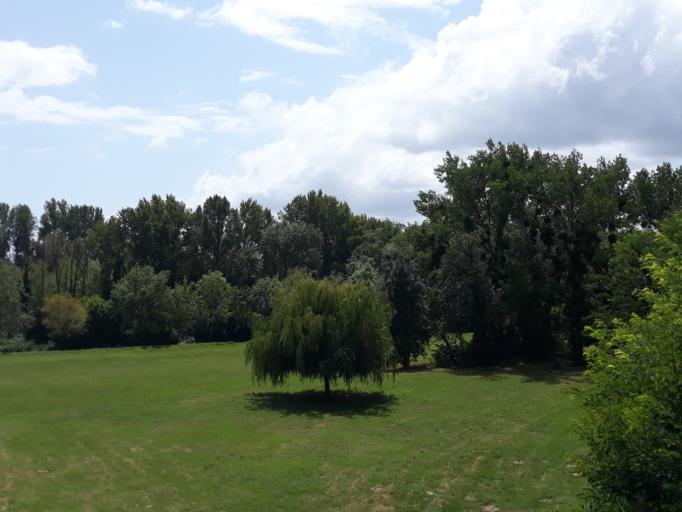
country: FR
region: Aquitaine
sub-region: Departement de la Gironde
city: Saint-Macaire
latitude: 44.5634
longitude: -0.2259
